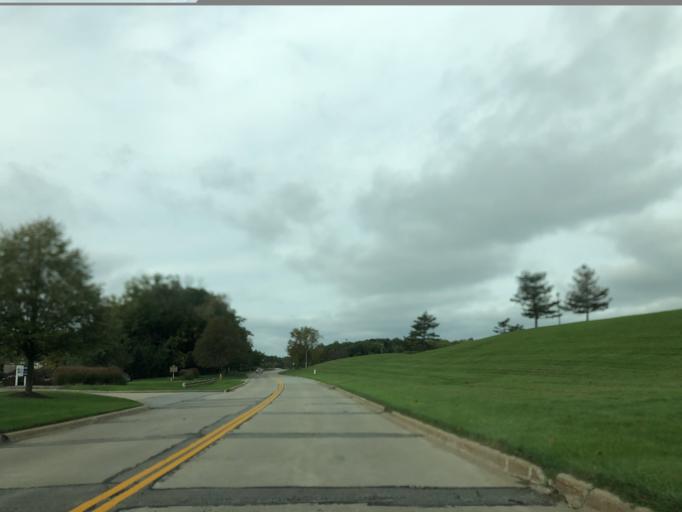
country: US
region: Ohio
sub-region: Cuyahoga County
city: Brecksville
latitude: 41.2832
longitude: -81.6313
